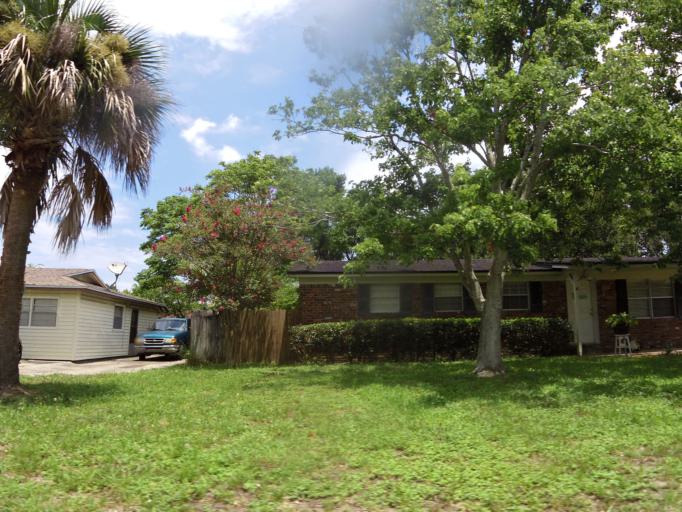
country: US
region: Florida
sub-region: Duval County
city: Atlantic Beach
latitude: 30.3307
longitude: -81.4101
